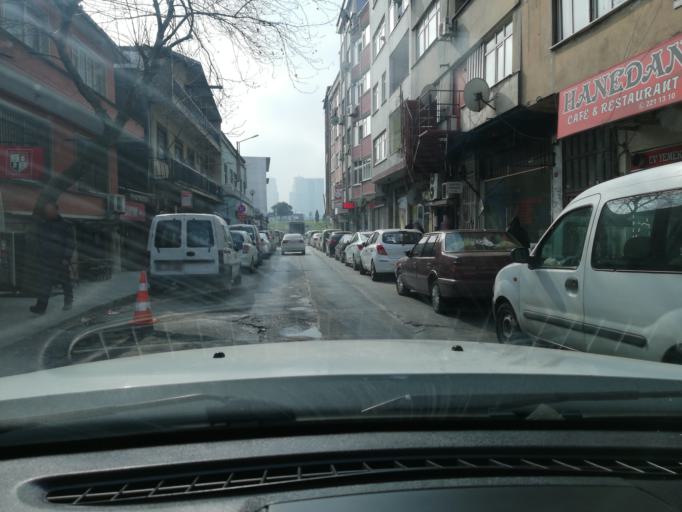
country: TR
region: Istanbul
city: Sisli
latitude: 41.0696
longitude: 28.9775
